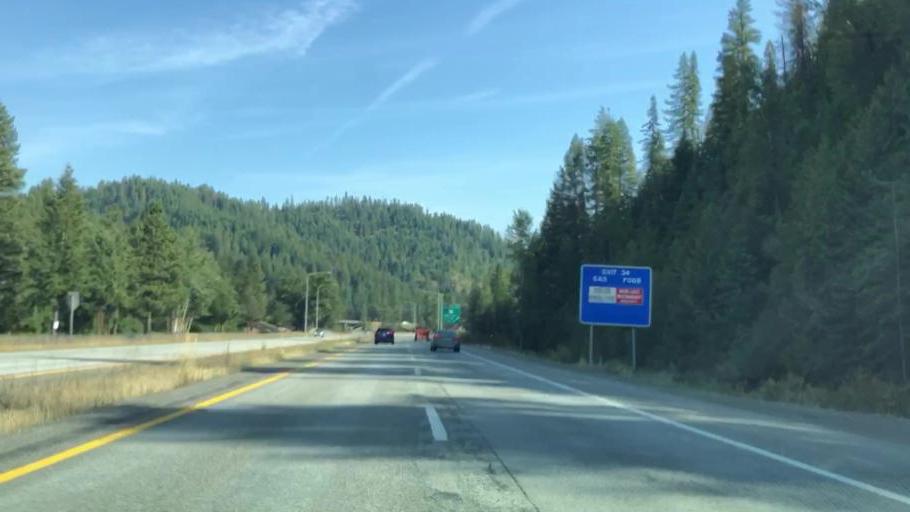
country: US
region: Idaho
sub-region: Shoshone County
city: Pinehurst
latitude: 47.5764
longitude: -116.4496
